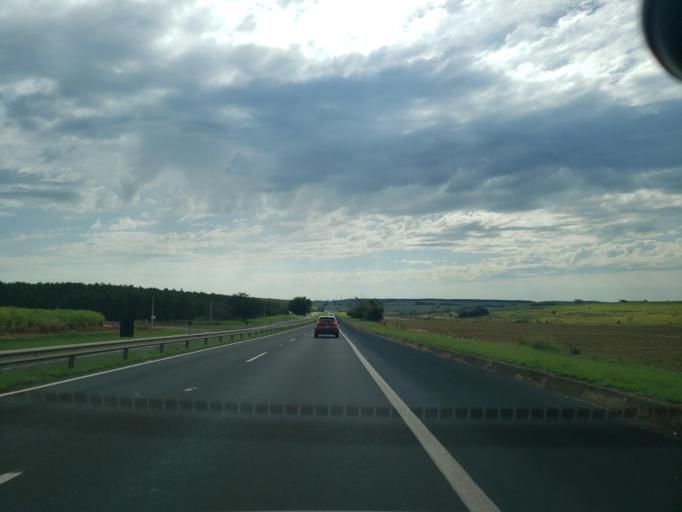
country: BR
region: Sao Paulo
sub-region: Cafelandia
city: Cafelandia
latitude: -21.7943
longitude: -49.6475
